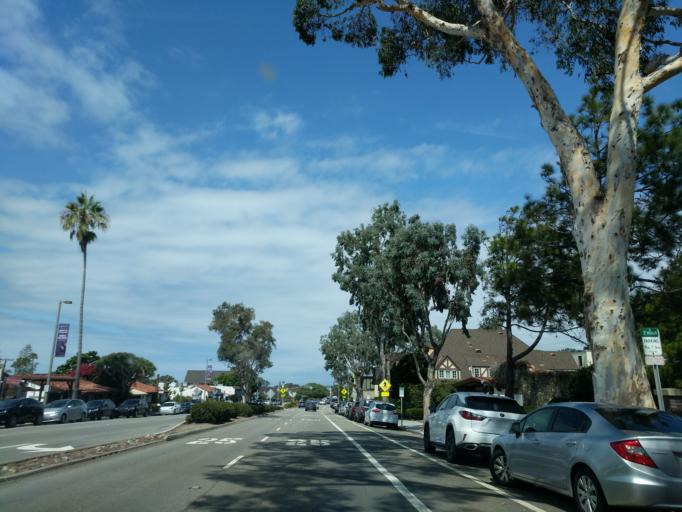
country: US
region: California
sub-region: San Diego County
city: Del Mar
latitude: 32.9577
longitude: -117.2646
